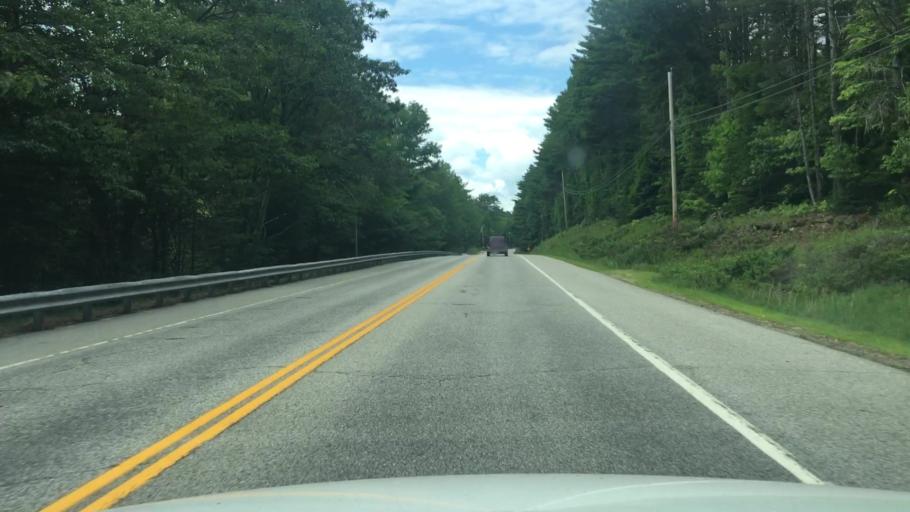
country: US
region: Maine
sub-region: Oxford County
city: West Paris
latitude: 44.3401
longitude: -70.5594
